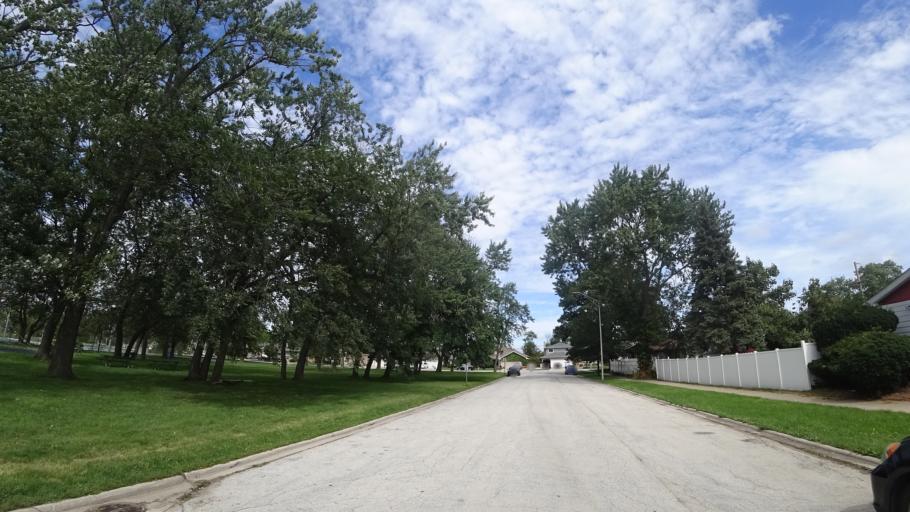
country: US
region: Illinois
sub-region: Cook County
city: Burbank
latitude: 41.7223
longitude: -87.7825
